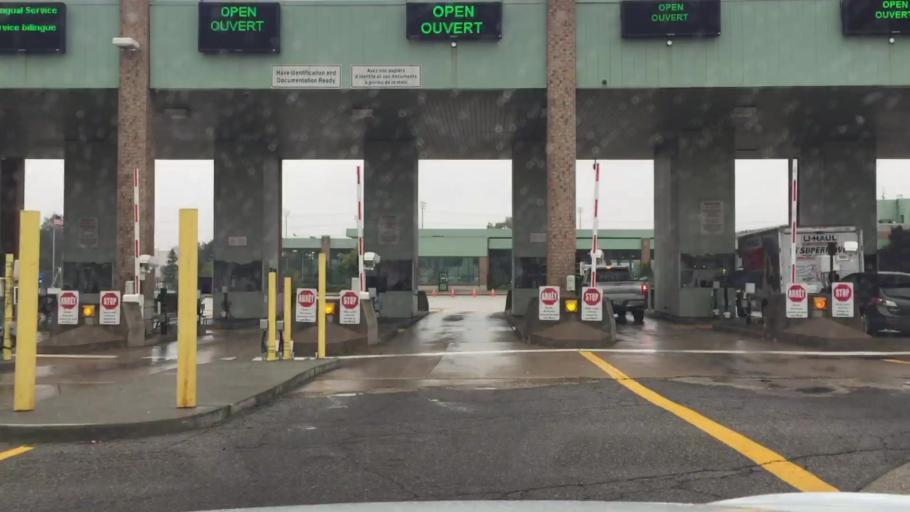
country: US
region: Michigan
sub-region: Wayne County
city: Detroit
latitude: 42.3017
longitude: -83.0657
